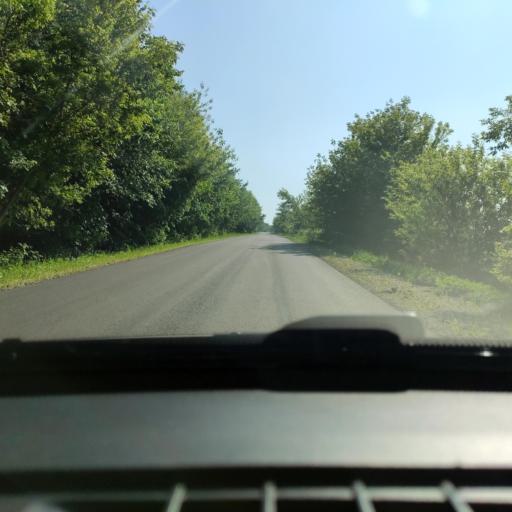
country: RU
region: Voronezj
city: Anna
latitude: 51.6327
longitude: 40.3537
